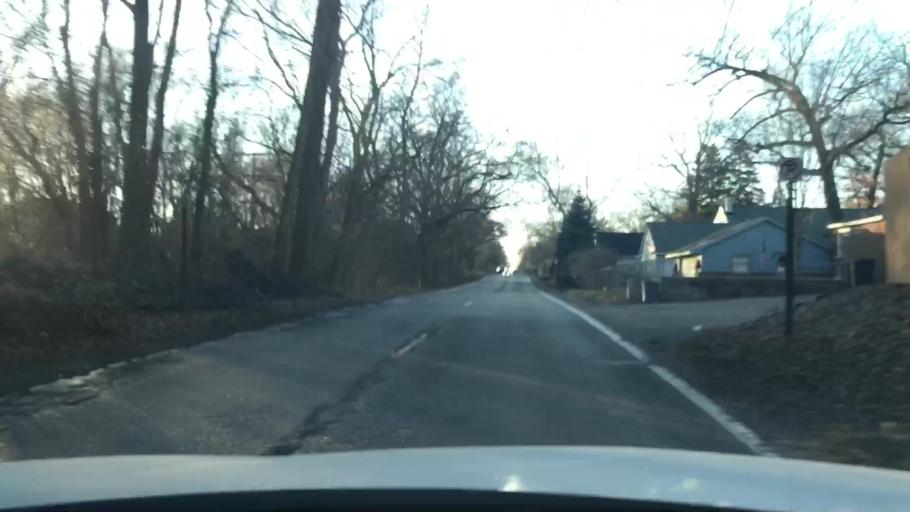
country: US
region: Michigan
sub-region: Oakland County
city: West Bloomfield Township
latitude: 42.5993
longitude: -83.4256
